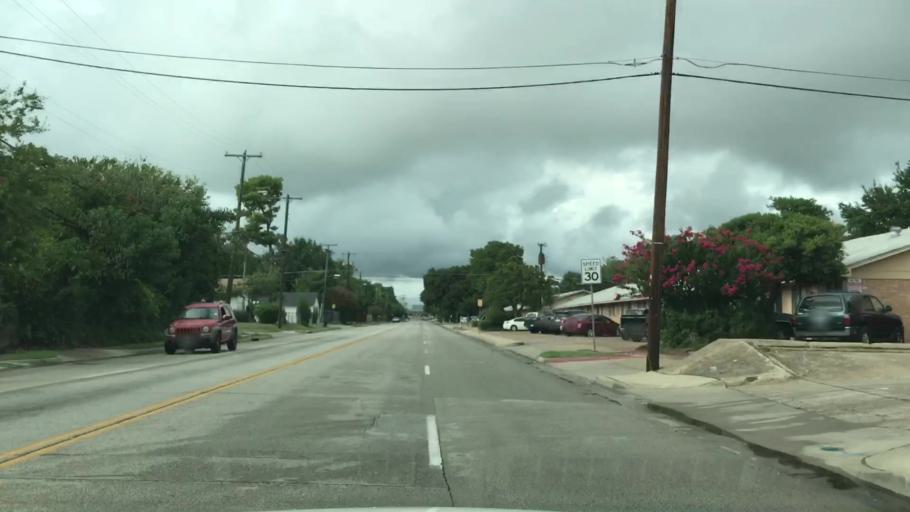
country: US
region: Texas
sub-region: Dallas County
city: Irving
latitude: 32.8299
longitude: -96.9303
